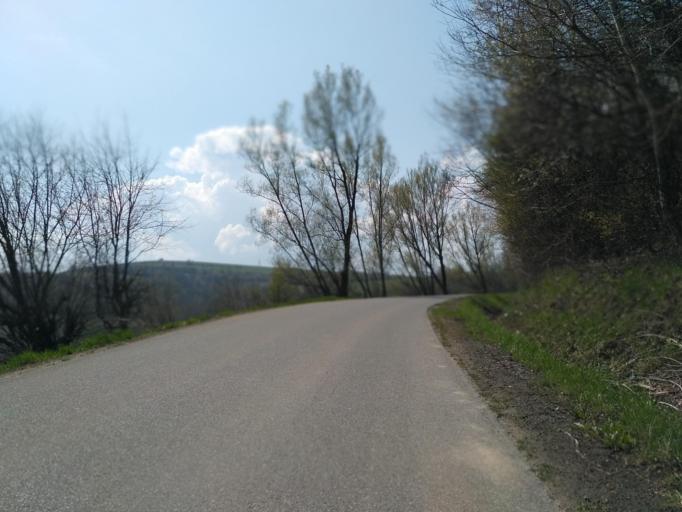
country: PL
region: Subcarpathian Voivodeship
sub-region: Powiat sanocki
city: Zarszyn
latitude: 49.5569
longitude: 21.9930
